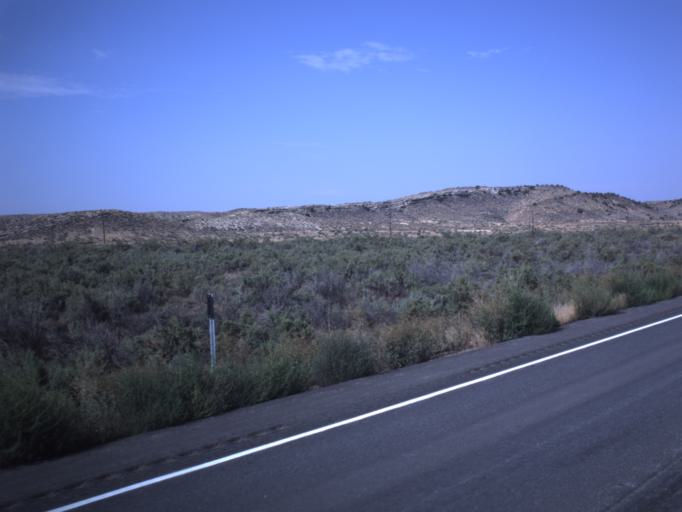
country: US
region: Utah
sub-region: Uintah County
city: Naples
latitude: 40.2901
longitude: -109.1599
